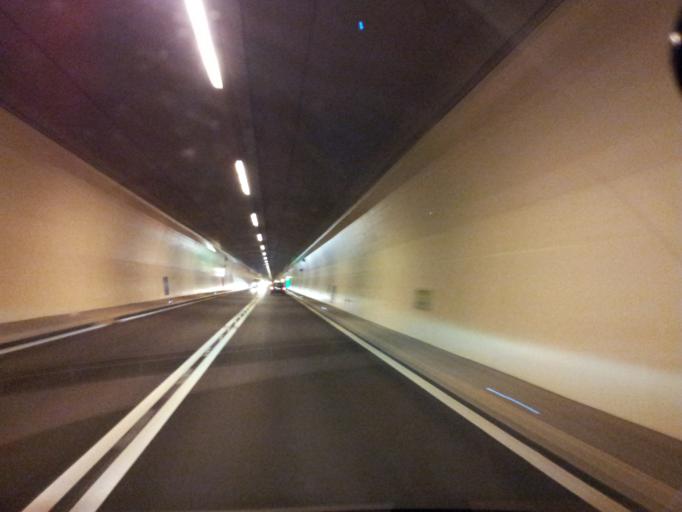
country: CH
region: Obwalden
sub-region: Obwalden
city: Giswil
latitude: 46.8287
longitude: 8.1883
